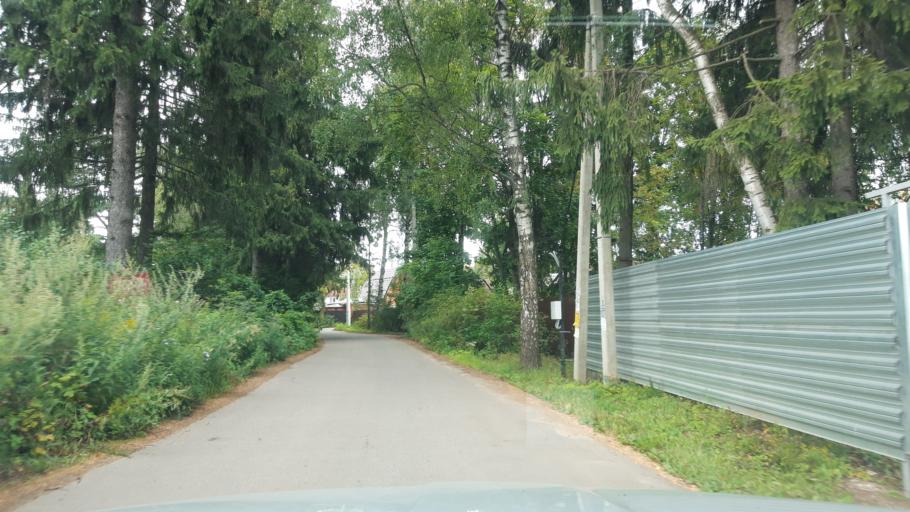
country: RU
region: Moskovskaya
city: Povarovo
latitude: 56.0619
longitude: 37.0695
